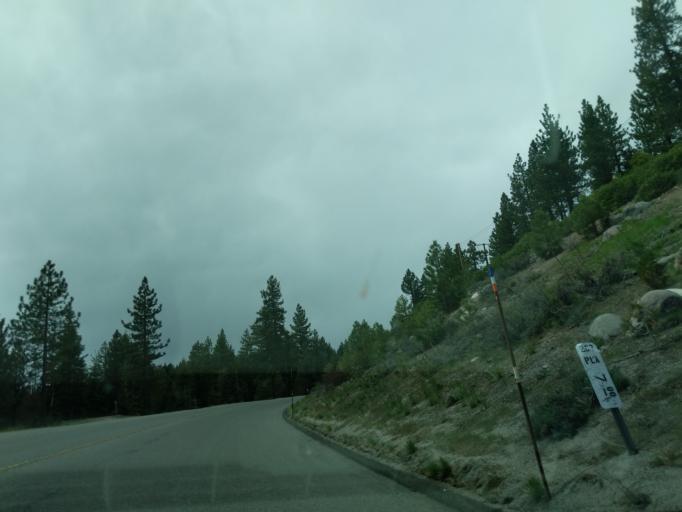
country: US
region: California
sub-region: Placer County
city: Tahoe Vista
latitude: 39.2585
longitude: -120.0677
